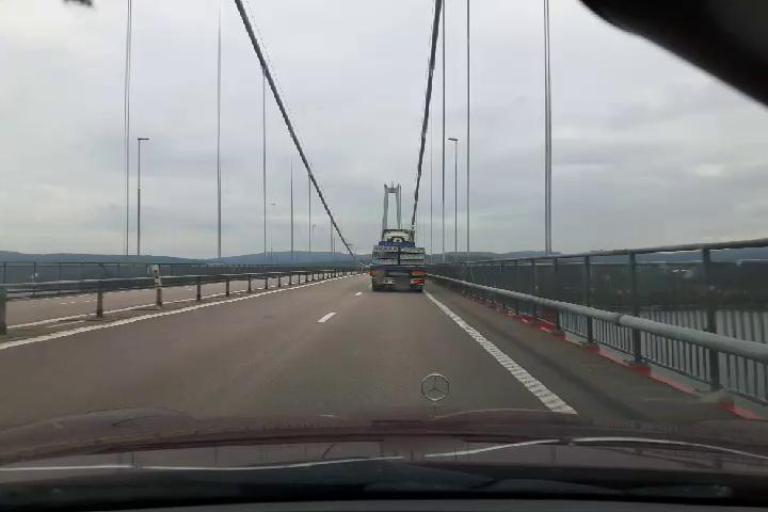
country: SE
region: Vaesternorrland
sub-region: Haernoesands Kommun
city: Haernoesand
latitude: 62.7980
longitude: 17.9383
